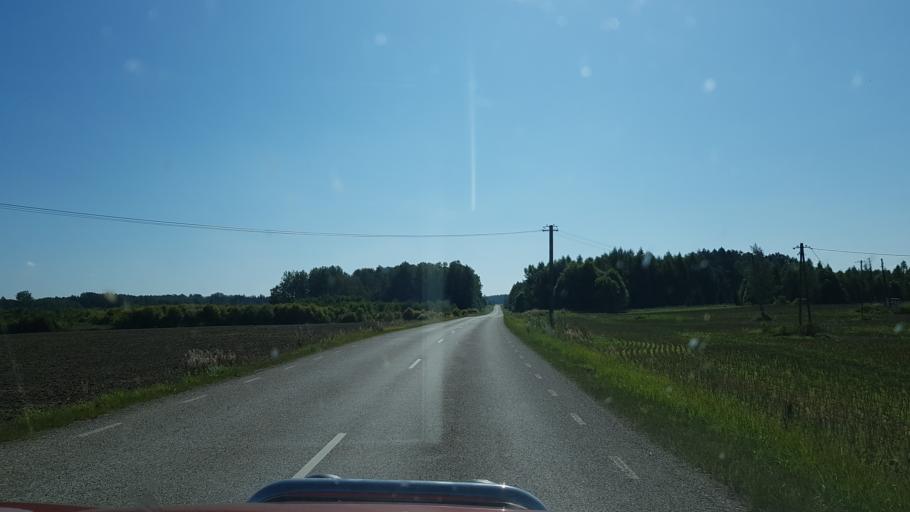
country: EE
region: Polvamaa
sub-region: Polva linn
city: Polva
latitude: 58.2344
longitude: 27.2185
